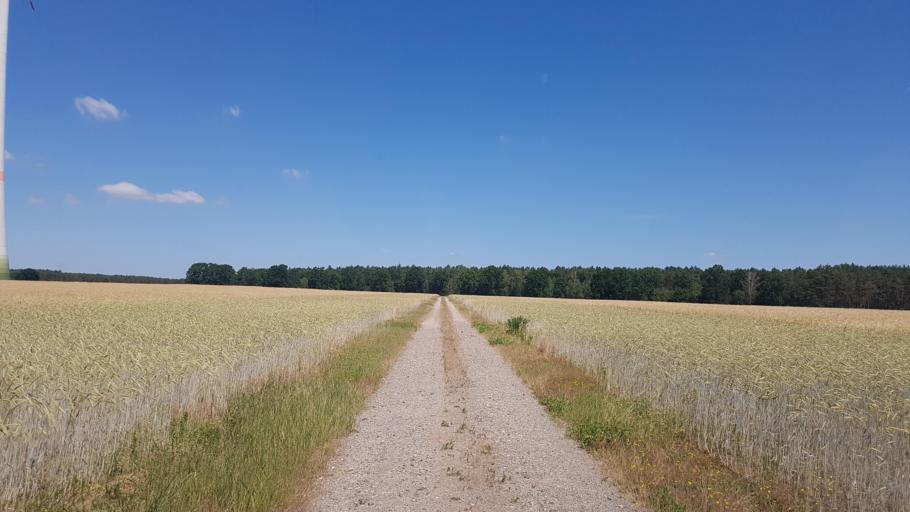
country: DE
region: Brandenburg
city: Treuenbrietzen
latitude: 52.0221
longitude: 12.8579
